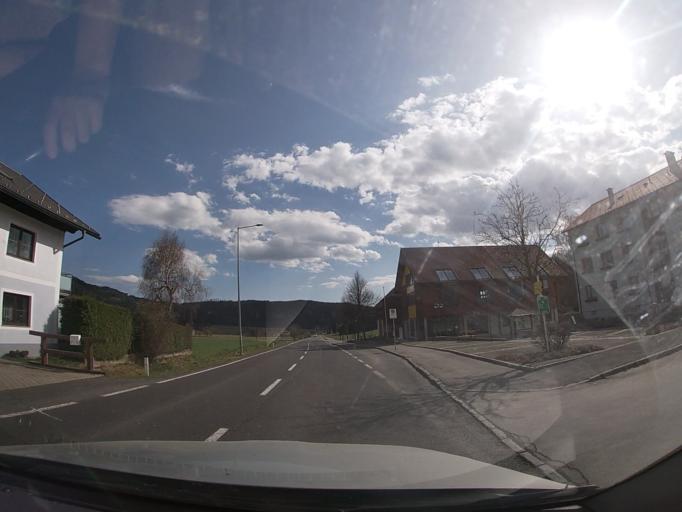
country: AT
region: Styria
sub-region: Politischer Bezirk Murau
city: Perchau am Sattel
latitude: 47.1078
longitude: 14.4572
